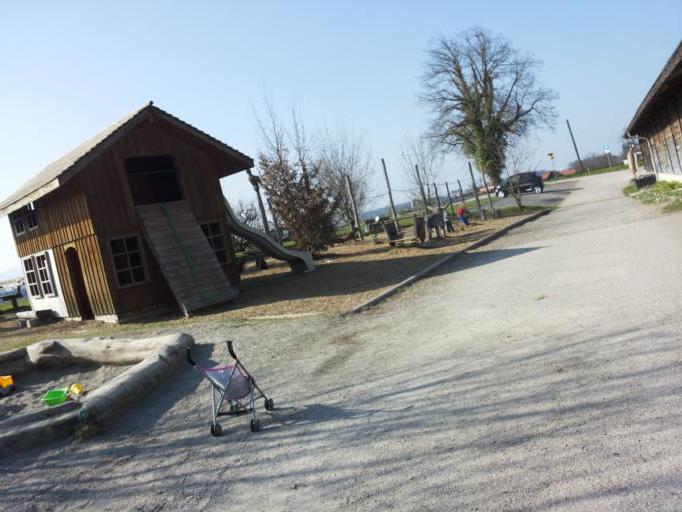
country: CH
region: Zug
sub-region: Zug
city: Cham
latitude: 47.1869
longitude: 8.4638
